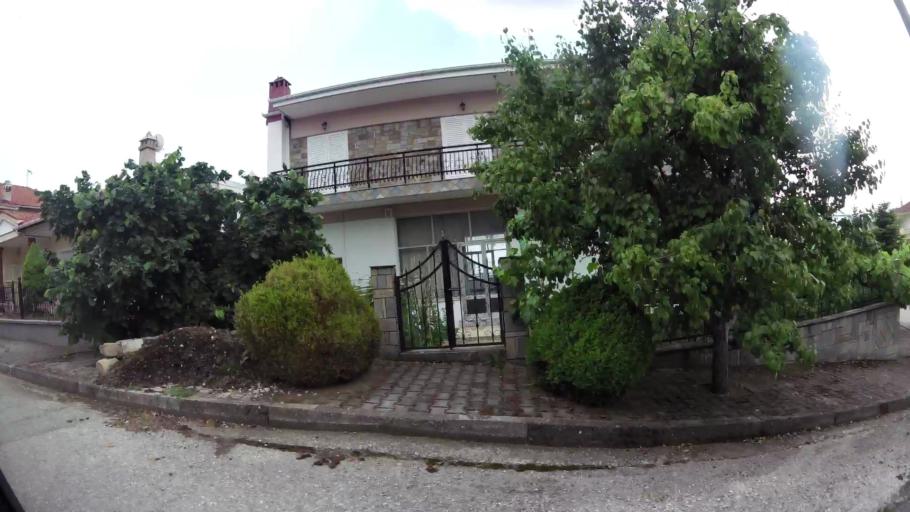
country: GR
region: West Macedonia
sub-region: Nomos Kozanis
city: Koila
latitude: 40.3221
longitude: 21.8210
